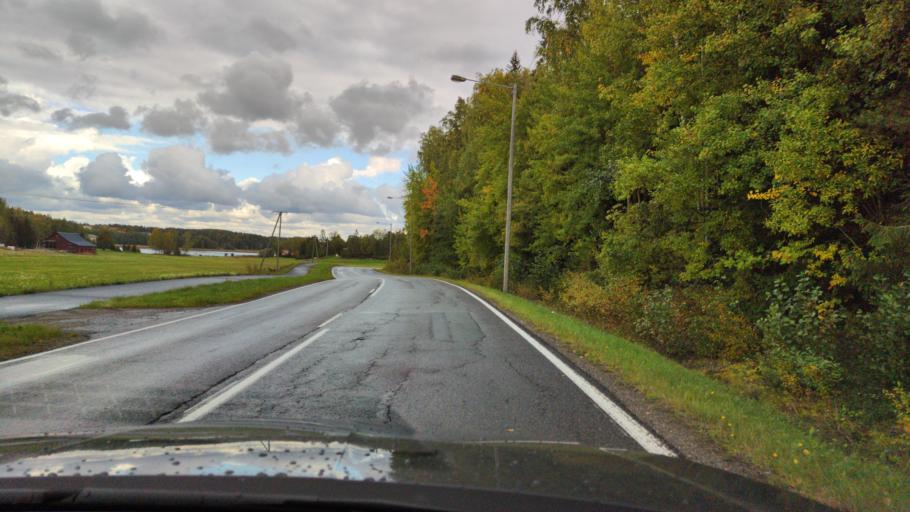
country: FI
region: Varsinais-Suomi
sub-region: Turku
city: Turku
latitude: 60.3628
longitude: 22.1938
